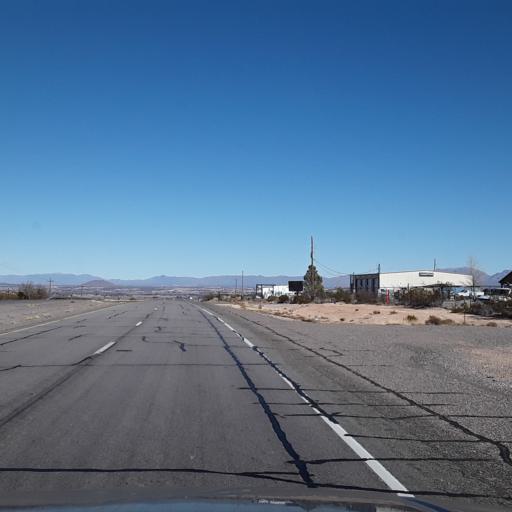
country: US
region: New Mexico
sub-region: Dona Ana County
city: Mesilla
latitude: 32.2861
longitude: -106.8763
